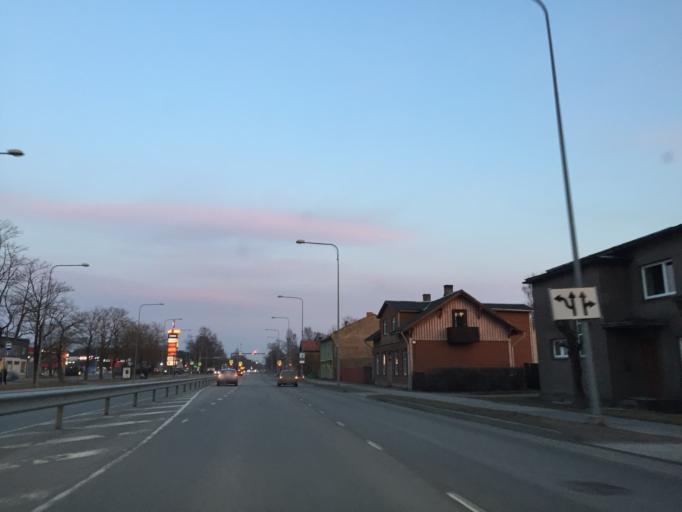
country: EE
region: Paernumaa
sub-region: Paernu linn
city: Parnu
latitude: 58.3714
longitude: 24.5450
